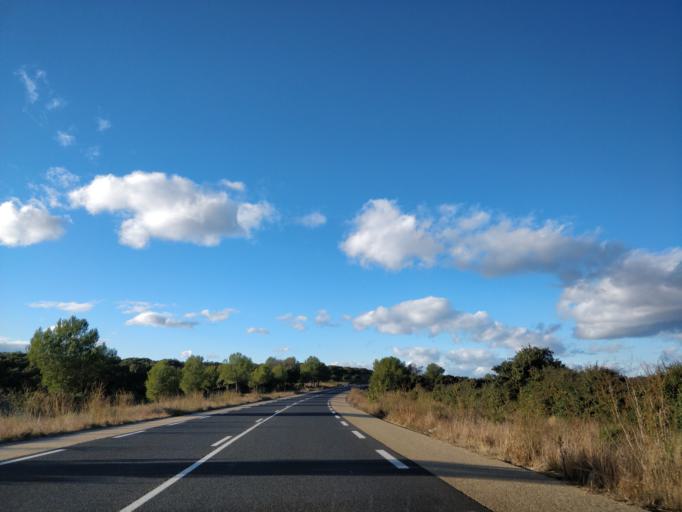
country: FR
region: Languedoc-Roussillon
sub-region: Departement de l'Herault
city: Teyran
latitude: 43.6766
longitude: 3.9502
